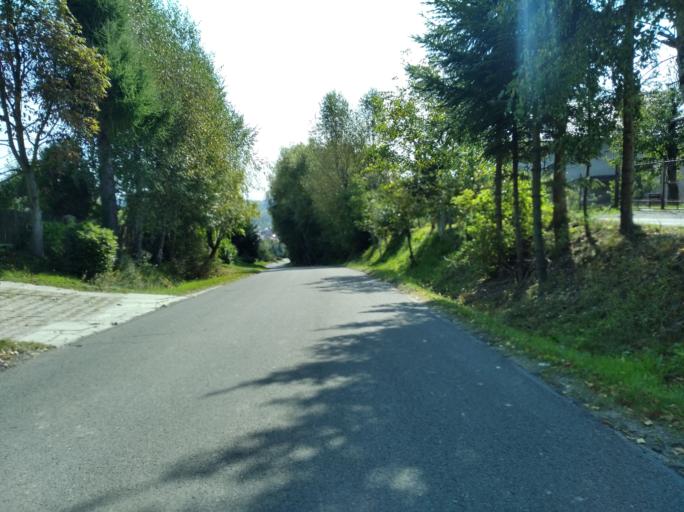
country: PL
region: Subcarpathian Voivodeship
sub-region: Powiat strzyzowski
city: Czudec
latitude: 49.9507
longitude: 21.8339
